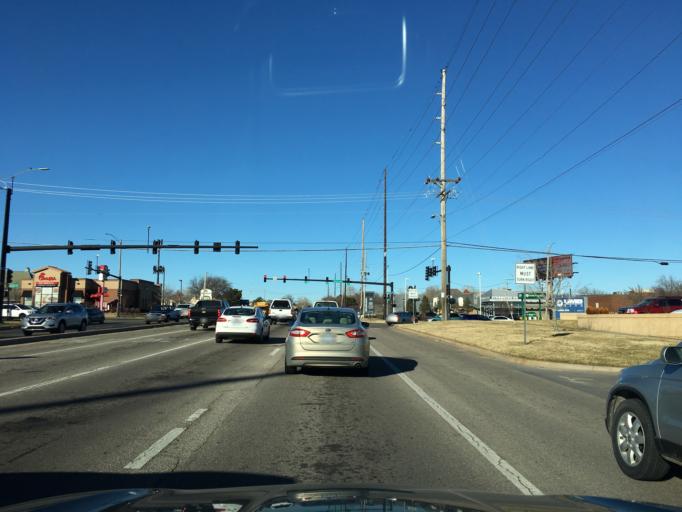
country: US
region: Kansas
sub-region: Sedgwick County
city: Bellaire
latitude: 37.6931
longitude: -97.2445
